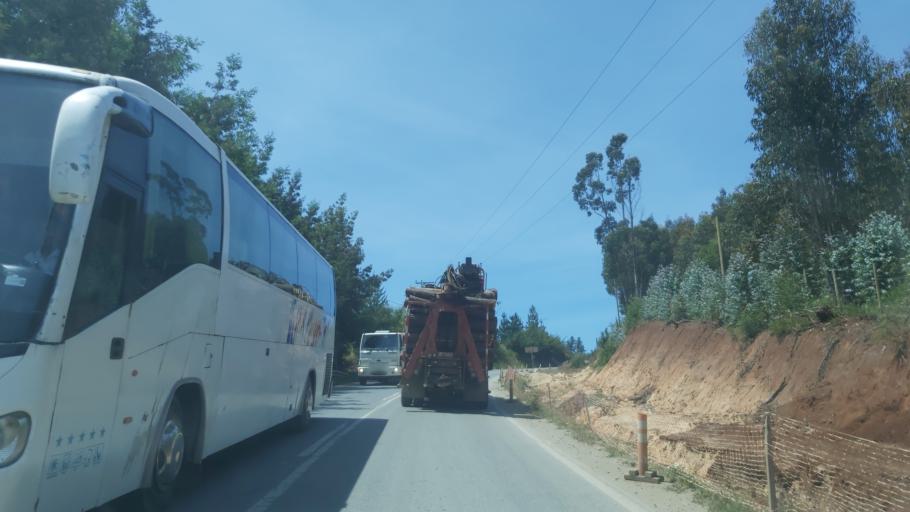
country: CL
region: Maule
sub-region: Provincia de Talca
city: Constitucion
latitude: -35.4438
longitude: -72.4636
